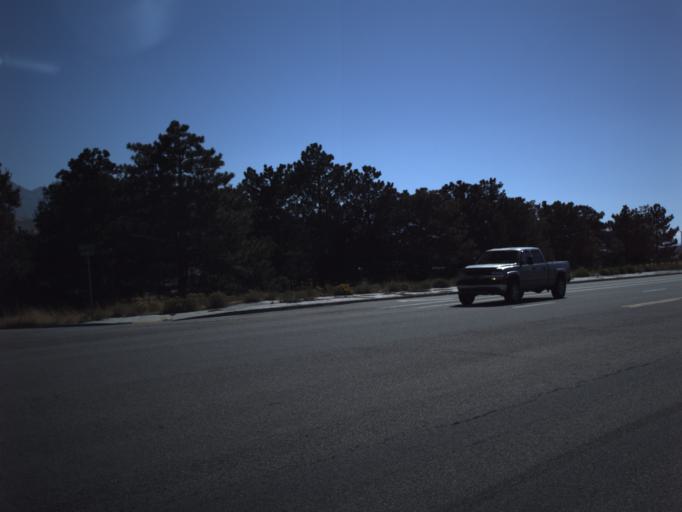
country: US
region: Utah
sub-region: Salt Lake County
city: Bluffdale
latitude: 40.4650
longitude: -111.9441
